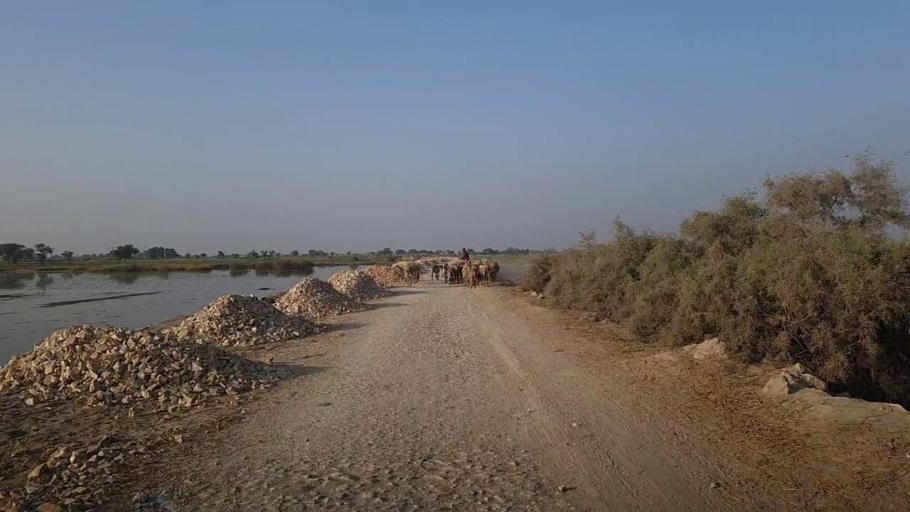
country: PK
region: Sindh
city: Tangwani
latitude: 28.2473
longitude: 69.0690
